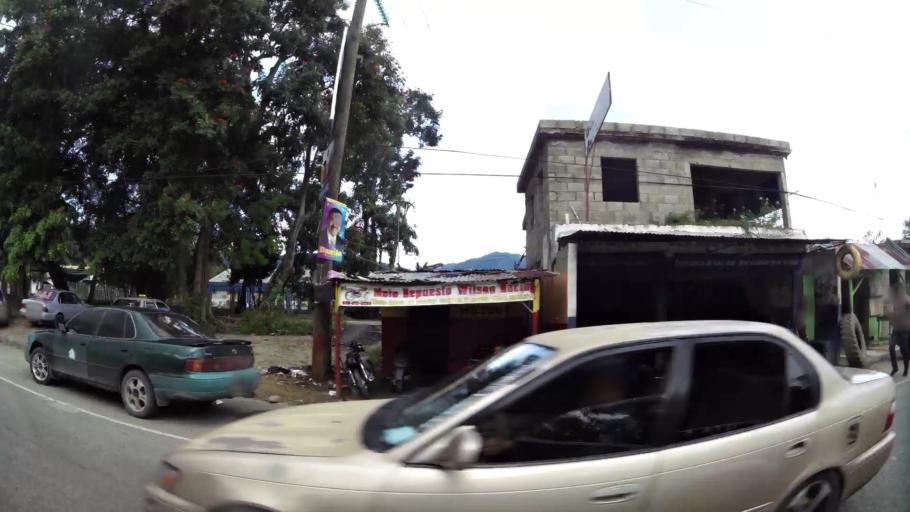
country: DO
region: San Cristobal
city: Villa Altagracia
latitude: 18.6857
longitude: -70.1808
